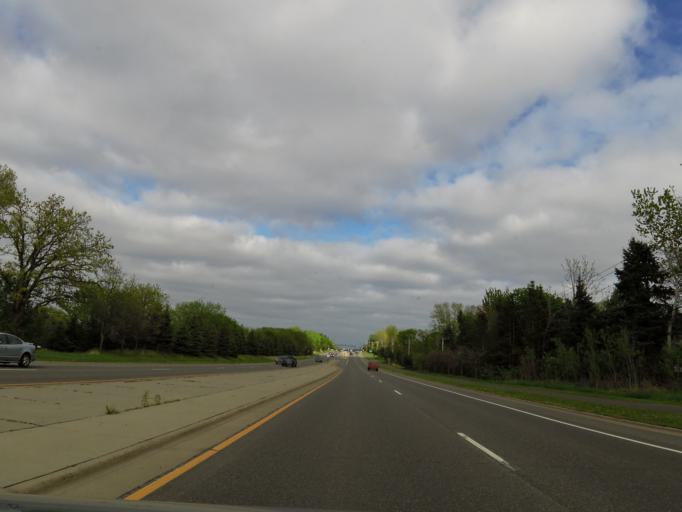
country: US
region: Minnesota
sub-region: Washington County
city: Woodbury
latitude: 44.9197
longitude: -92.9245
